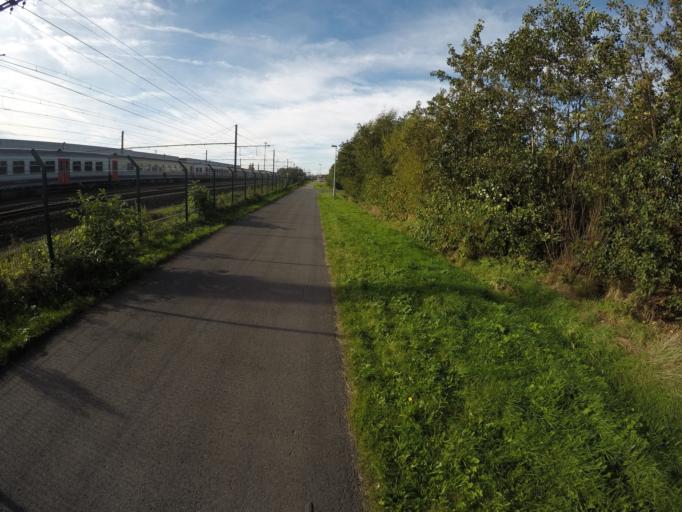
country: BE
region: Flanders
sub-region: Provincie Oost-Vlaanderen
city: Sint-Niklaas
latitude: 51.1795
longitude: 4.1676
